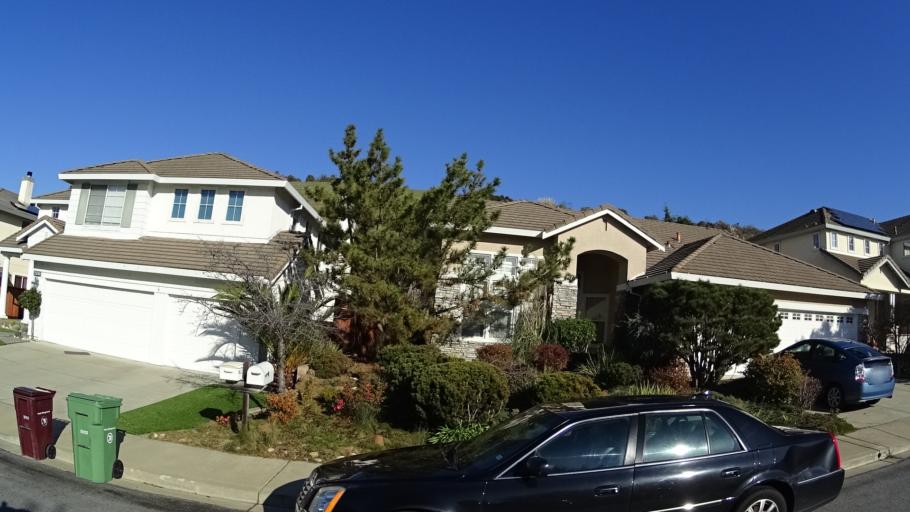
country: US
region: California
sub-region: Alameda County
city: Fairview
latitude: 37.6884
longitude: -122.0332
